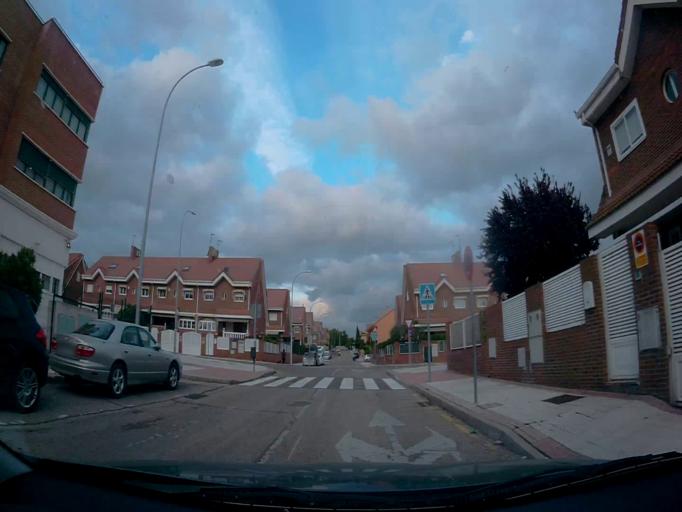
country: ES
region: Madrid
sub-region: Provincia de Madrid
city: Alcorcon
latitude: 40.3353
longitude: -3.8281
